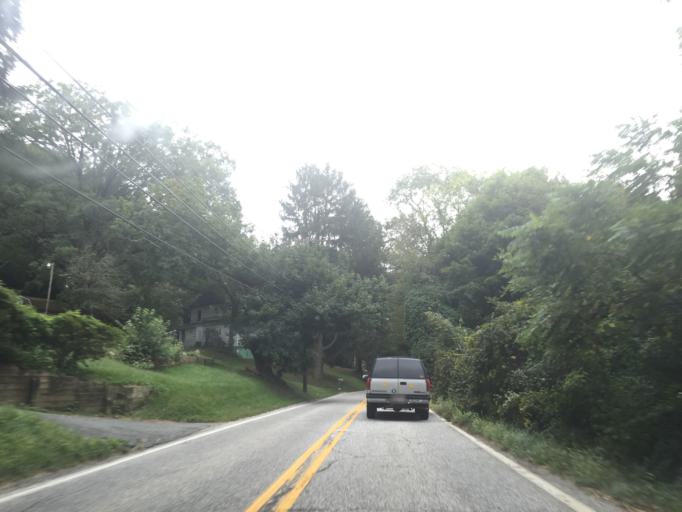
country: US
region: Maryland
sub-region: Baltimore County
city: Perry Hall
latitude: 39.4541
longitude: -76.4910
